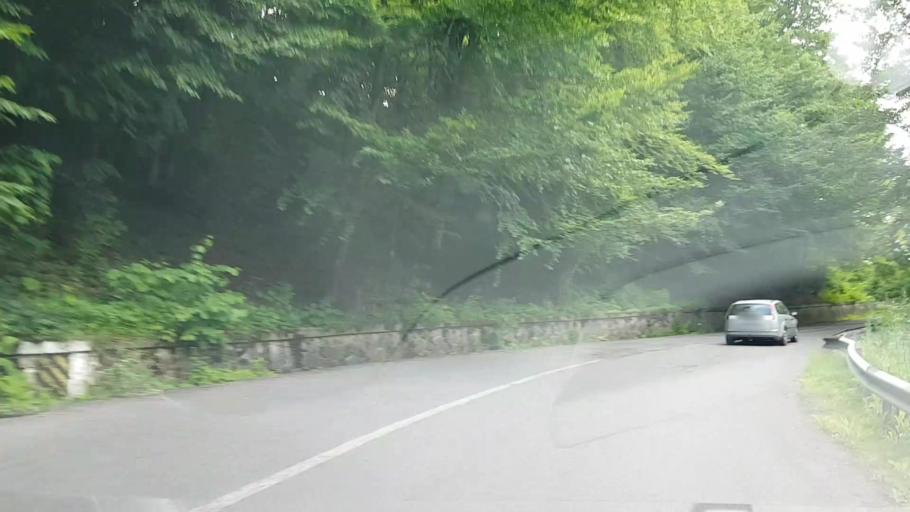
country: RO
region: Neamt
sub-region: Comuna Pangarati
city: Pangarati
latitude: 46.9450
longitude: 26.1289
